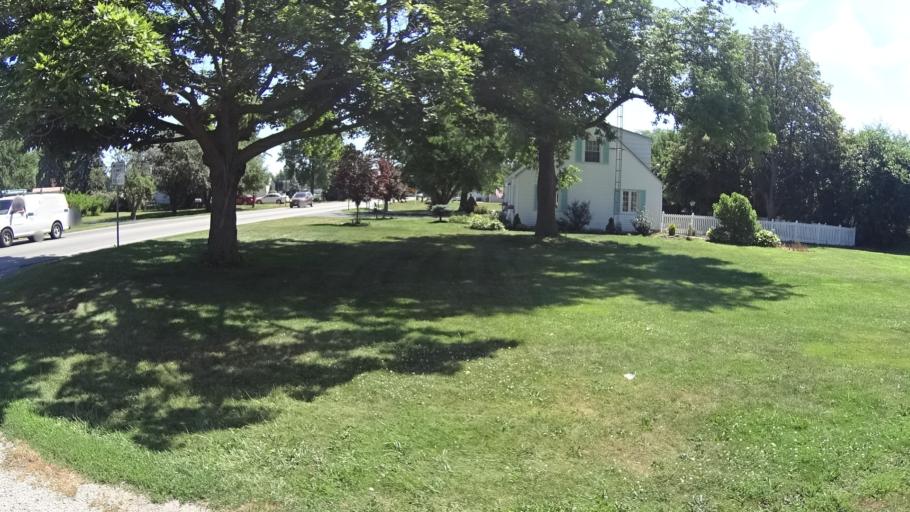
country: US
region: Ohio
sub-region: Erie County
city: Sandusky
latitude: 41.4084
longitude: -82.7027
